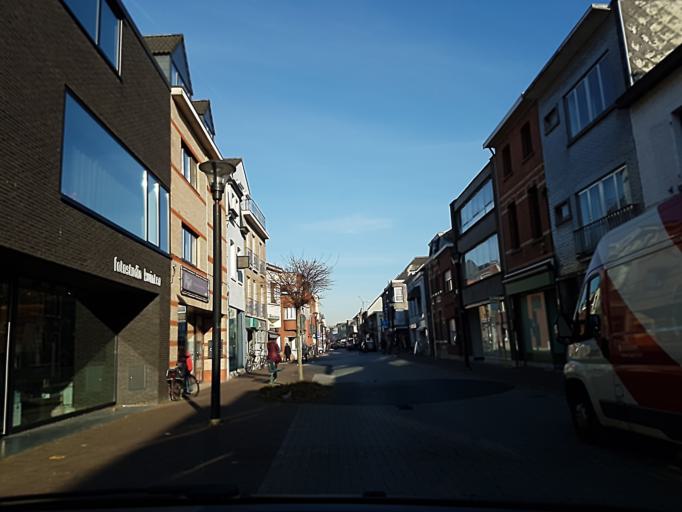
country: BE
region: Flanders
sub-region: Provincie Antwerpen
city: Willebroek
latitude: 51.0583
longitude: 4.3594
